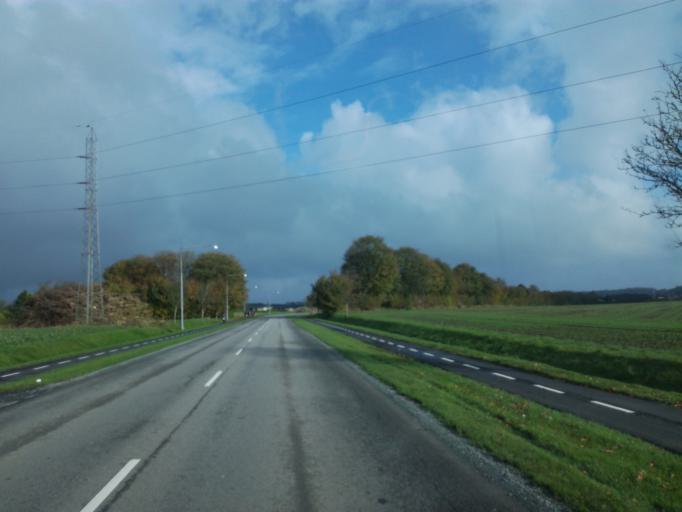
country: DK
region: South Denmark
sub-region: Vejle Kommune
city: Brejning
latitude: 55.6545
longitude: 9.6674
